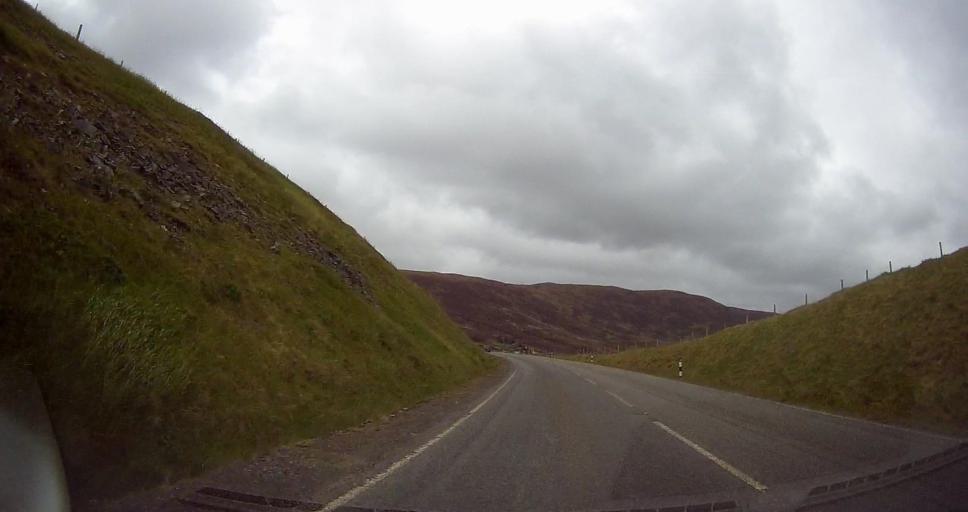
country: GB
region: Scotland
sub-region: Shetland Islands
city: Lerwick
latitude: 60.3704
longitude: -1.3131
